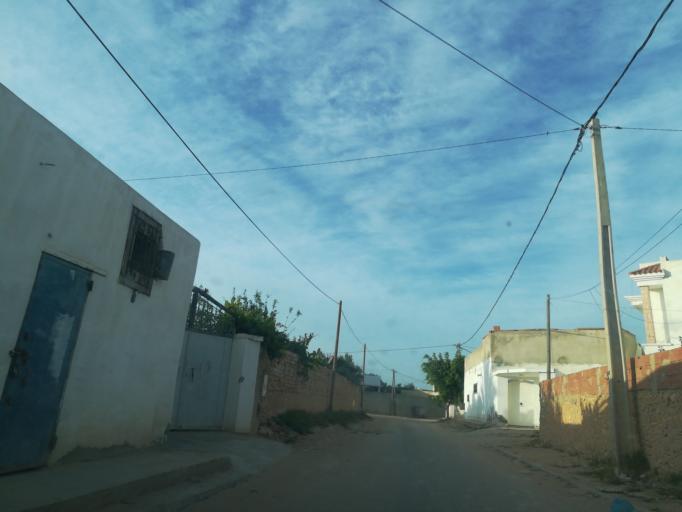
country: TN
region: Safaqis
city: Al Qarmadah
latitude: 34.8112
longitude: 10.7529
